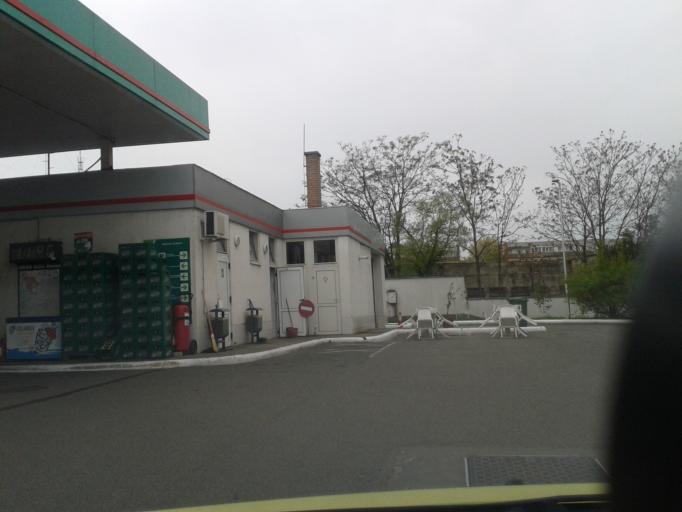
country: RO
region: Arad
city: Arad
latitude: 46.1814
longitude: 21.3308
